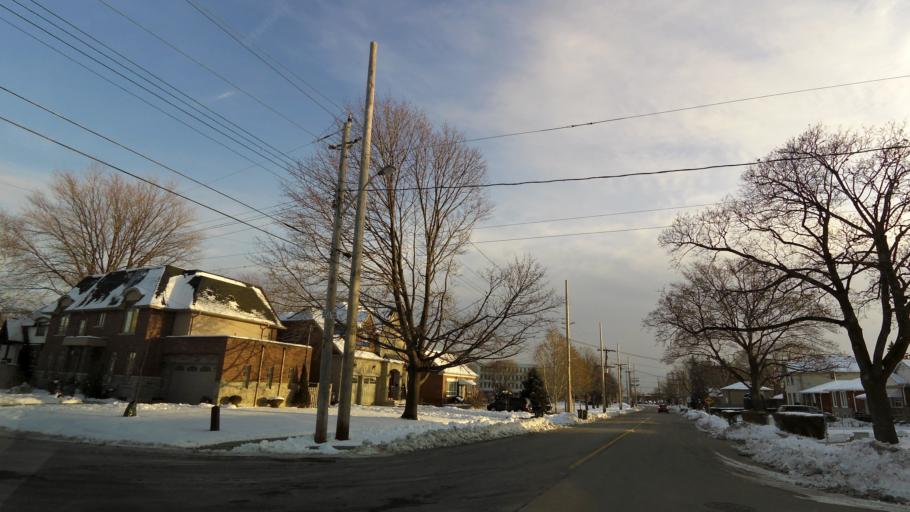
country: CA
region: Ontario
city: Etobicoke
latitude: 43.6346
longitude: -79.5462
